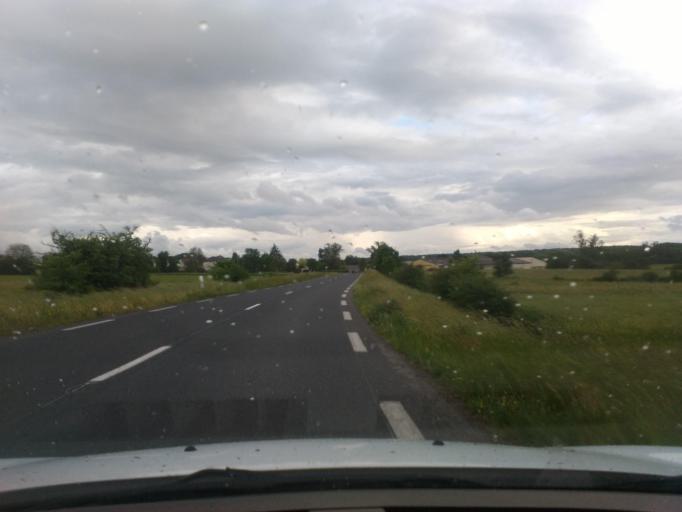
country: FR
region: Lorraine
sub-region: Departement de Meurthe-et-Moselle
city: Gerbeviller
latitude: 48.4541
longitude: 6.5625
